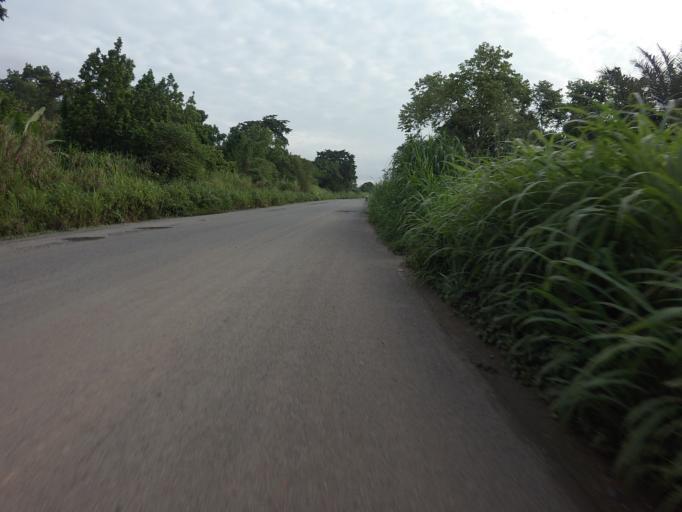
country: GH
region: Volta
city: Kpandu
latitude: 6.8703
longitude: 0.4171
